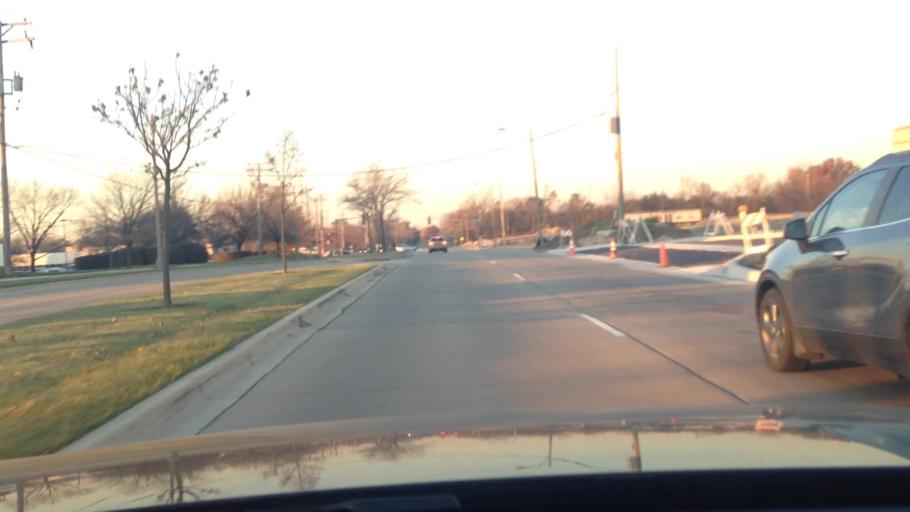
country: US
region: Illinois
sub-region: DuPage County
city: Lombard
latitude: 41.8482
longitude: -88.0264
